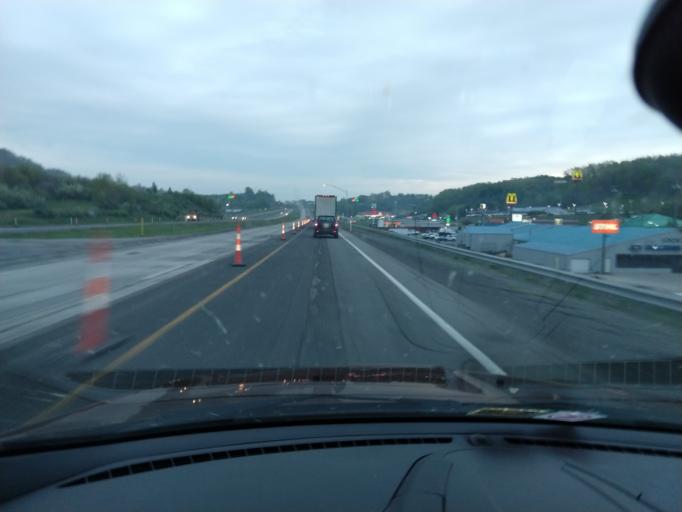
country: US
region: West Virginia
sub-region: Braxton County
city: Sutton
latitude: 38.6987
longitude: -80.6669
